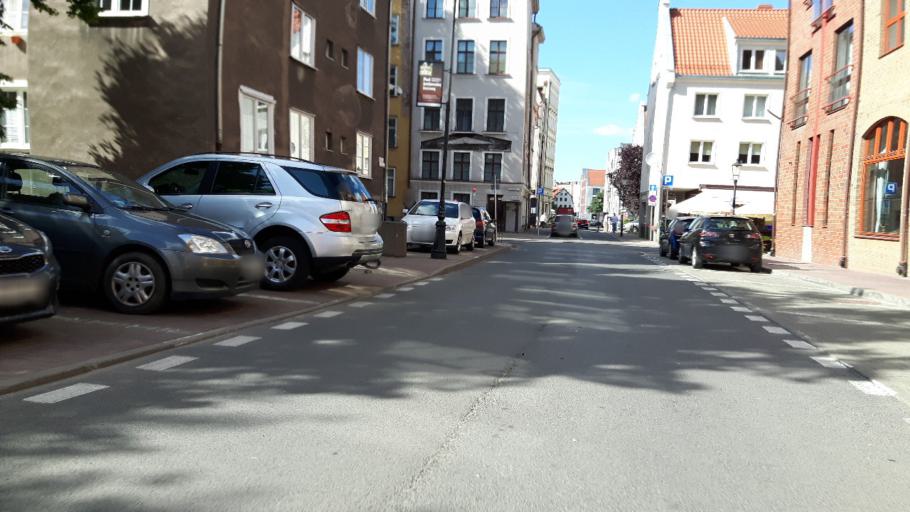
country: PL
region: Pomeranian Voivodeship
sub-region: Gdansk
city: Gdansk
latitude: 54.3511
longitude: 18.6572
